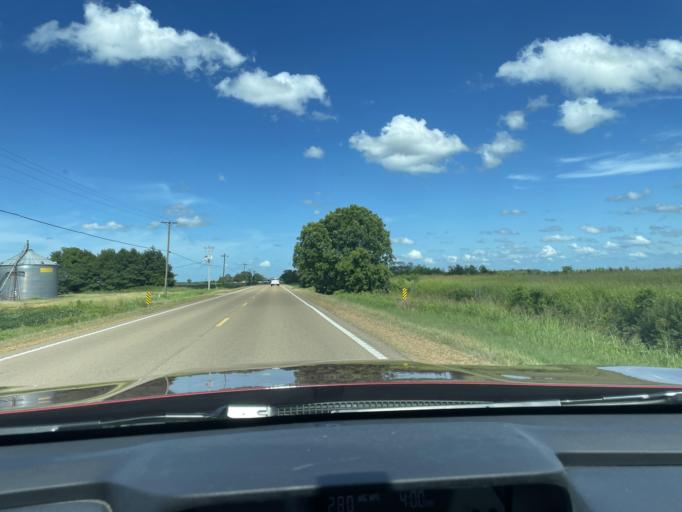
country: US
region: Mississippi
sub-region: Humphreys County
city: Belzoni
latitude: 33.1838
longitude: -90.5604
